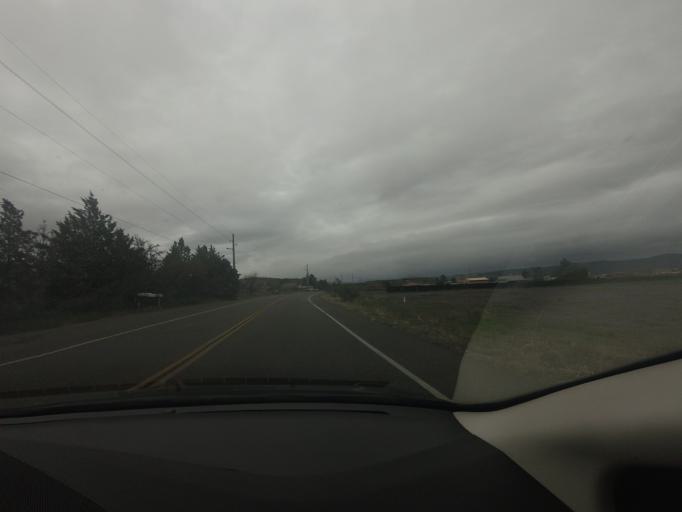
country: US
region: Arizona
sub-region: Yavapai County
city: Lake Montezuma
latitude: 34.6509
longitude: -111.7840
